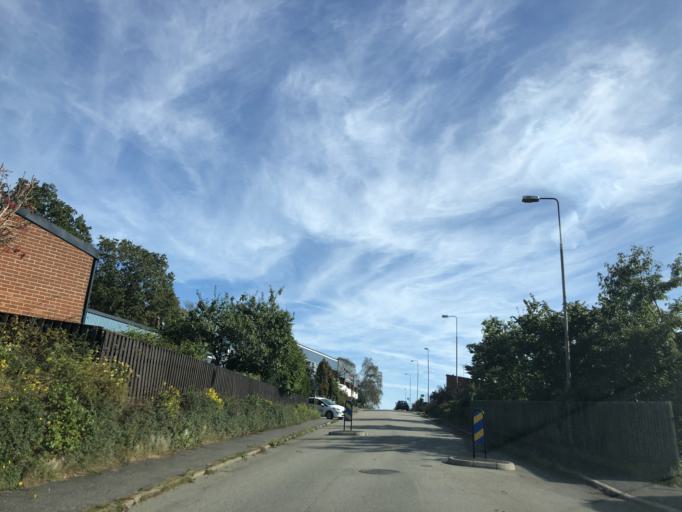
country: SE
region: Vaestra Goetaland
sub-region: Molndal
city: Moelndal
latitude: 57.6666
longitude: 12.0472
